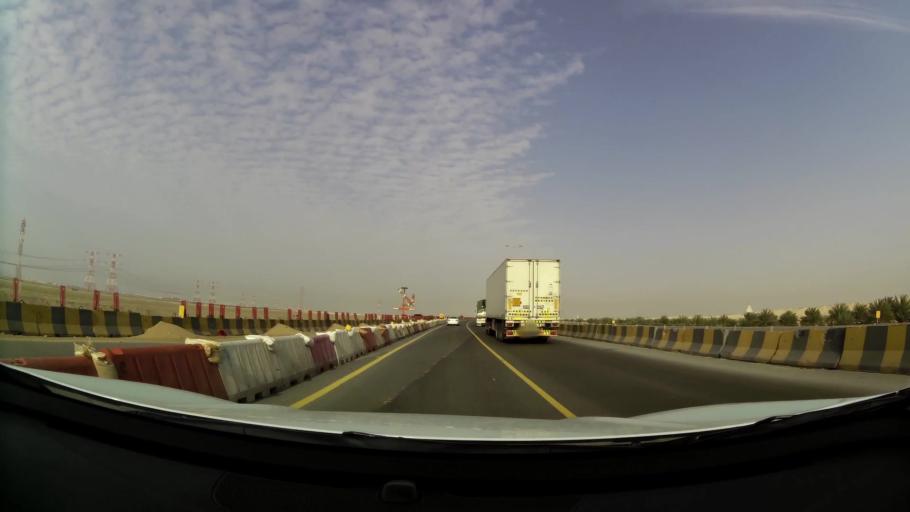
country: AE
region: Abu Dhabi
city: Abu Dhabi
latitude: 24.2225
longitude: 54.4356
